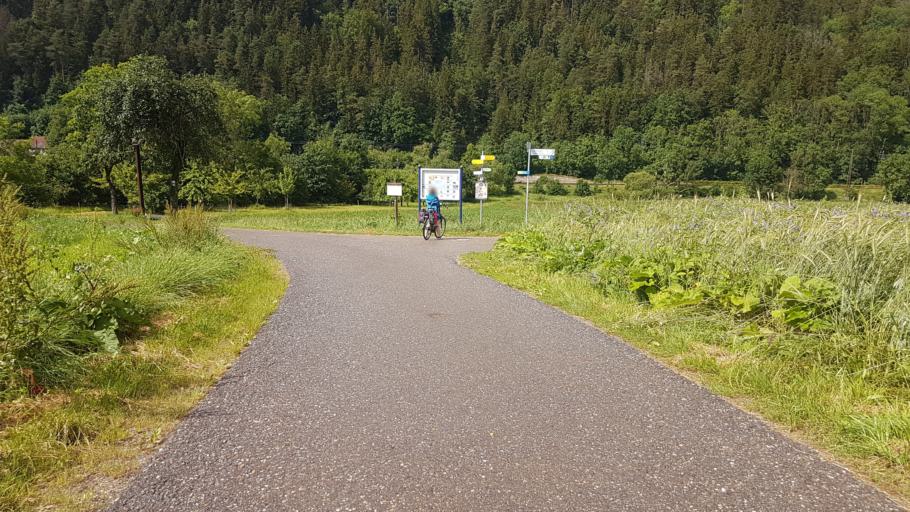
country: DE
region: Baden-Wuerttemberg
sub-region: Tuebingen Region
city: Leibertingen
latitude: 48.0711
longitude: 9.0125
